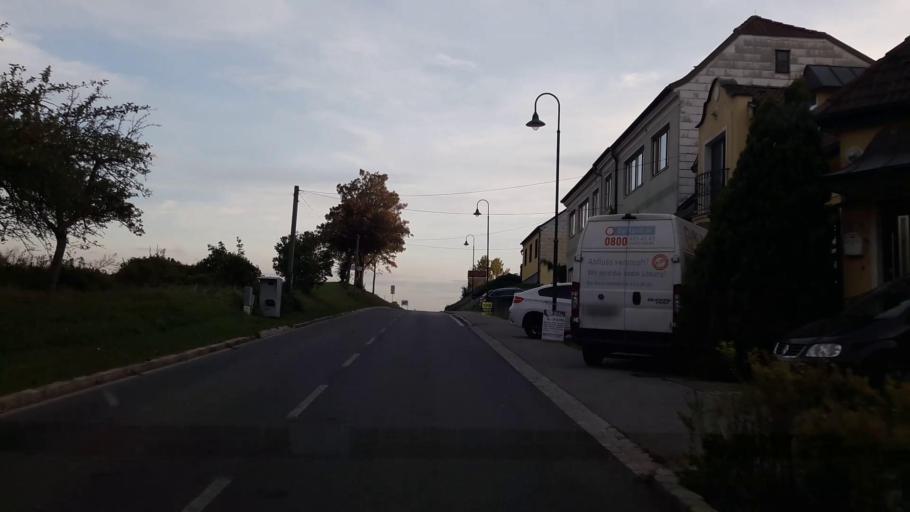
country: AT
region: Lower Austria
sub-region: Politischer Bezirk Korneuburg
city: Grossrussbach
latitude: 48.4588
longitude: 16.3732
